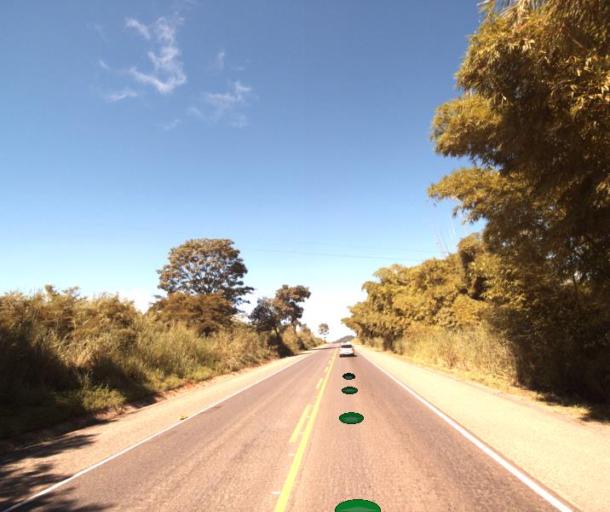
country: BR
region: Goias
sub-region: Ceres
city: Ceres
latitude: -15.2213
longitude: -49.5520
